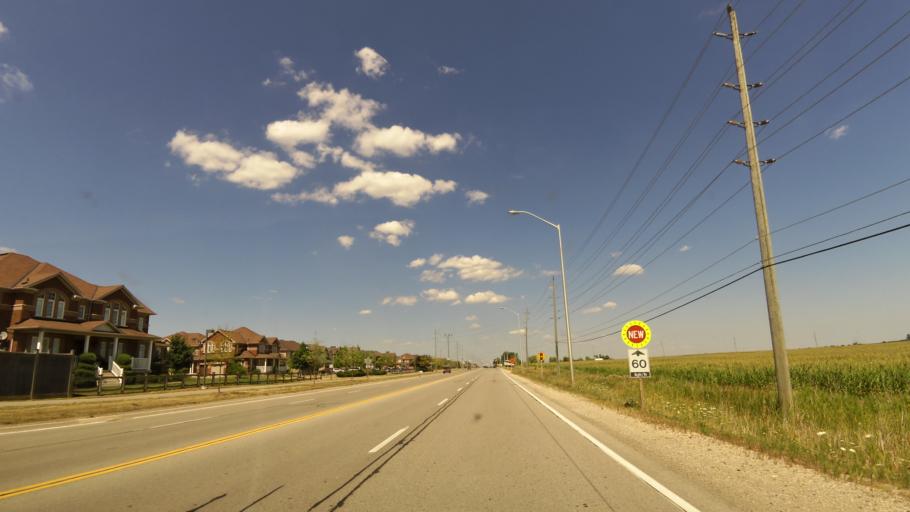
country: CA
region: Ontario
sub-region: Halton
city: Milton
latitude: 43.6252
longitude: -79.8760
